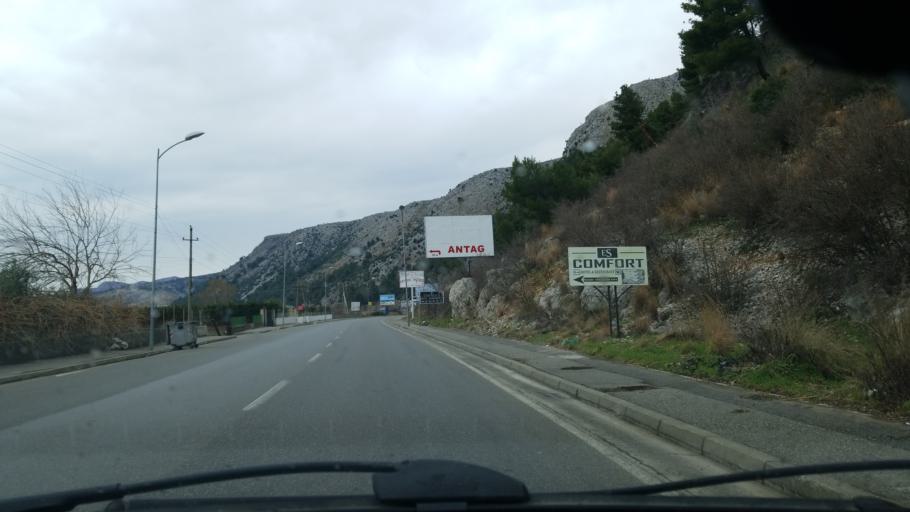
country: AL
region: Lezhe
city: Shengjin
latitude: 41.7997
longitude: 19.6174
